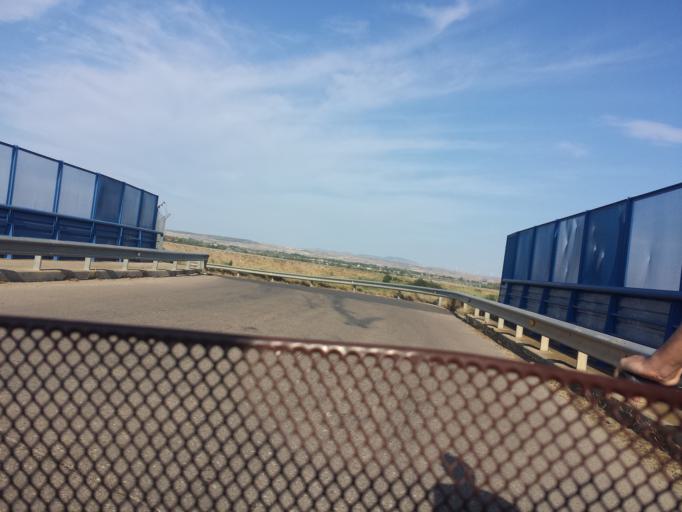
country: ES
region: Aragon
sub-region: Provincia de Zaragoza
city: Zaragoza
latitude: 41.7069
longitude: -0.8506
